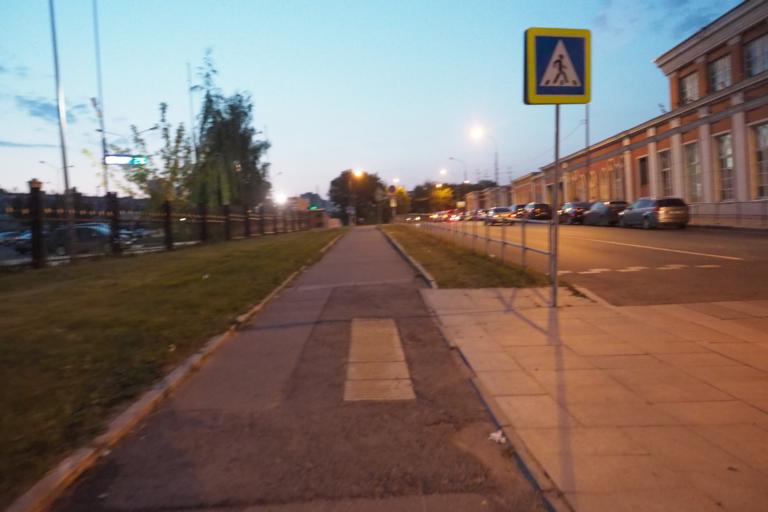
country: RU
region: Moscow
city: Orekhovo-Borisovo Severnoye
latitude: 55.6178
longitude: 37.6730
